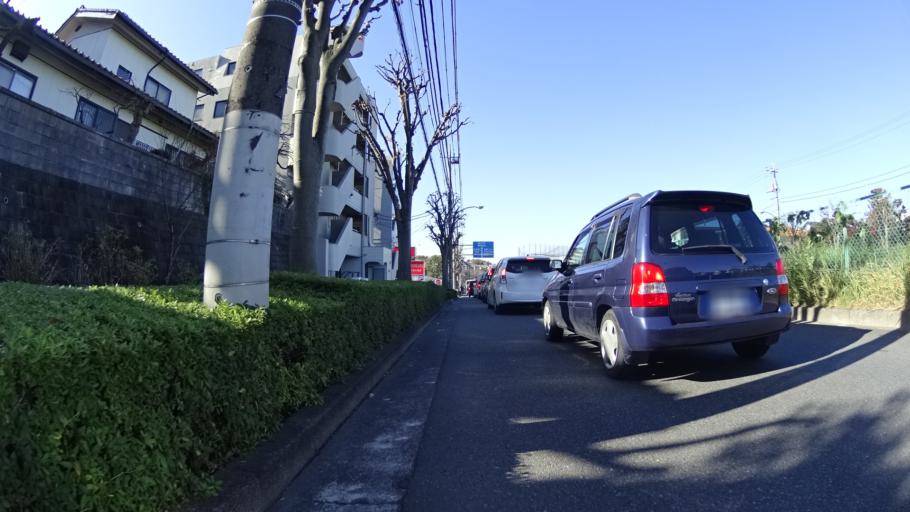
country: JP
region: Tokyo
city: Hino
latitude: 35.6088
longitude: 139.4283
